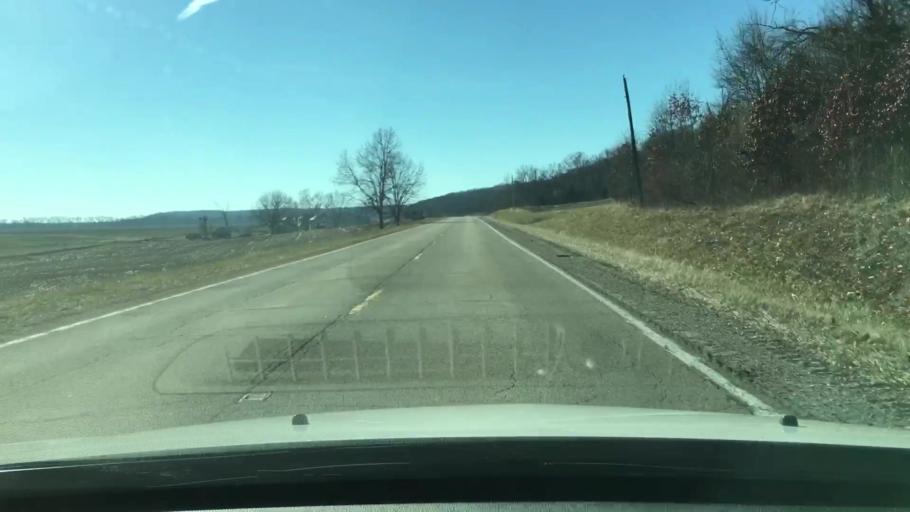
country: US
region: Illinois
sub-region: Mason County
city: Havana
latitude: 40.2501
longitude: -90.1846
